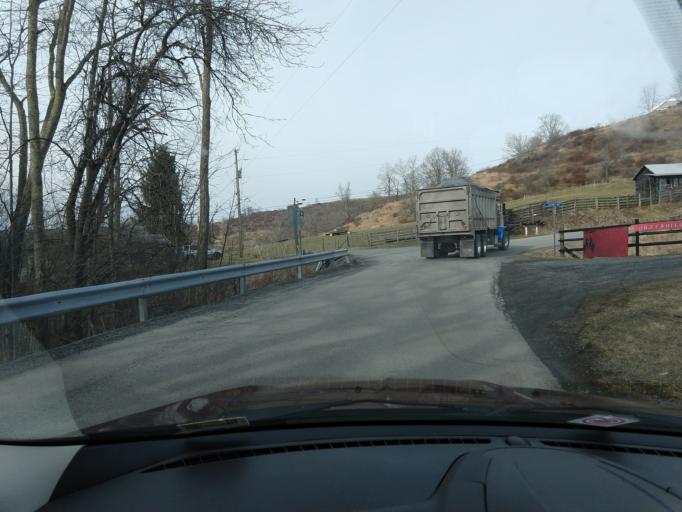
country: US
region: West Virginia
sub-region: Tucker County
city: Parsons
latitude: 39.0108
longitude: -79.5100
